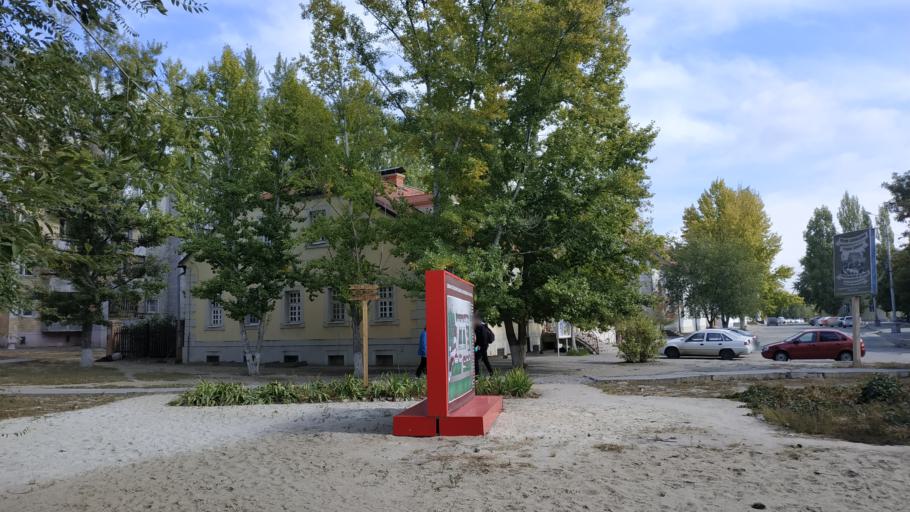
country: RU
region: Volgograd
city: Krasnoslobodsk
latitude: 48.5125
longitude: 44.5489
